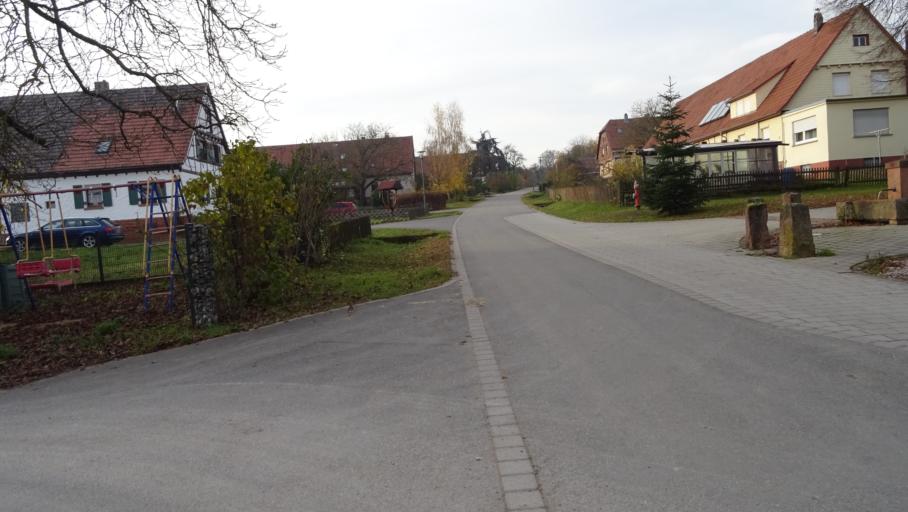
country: DE
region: Baden-Wuerttemberg
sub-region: Karlsruhe Region
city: Neckargerach
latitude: 49.4153
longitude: 9.0744
